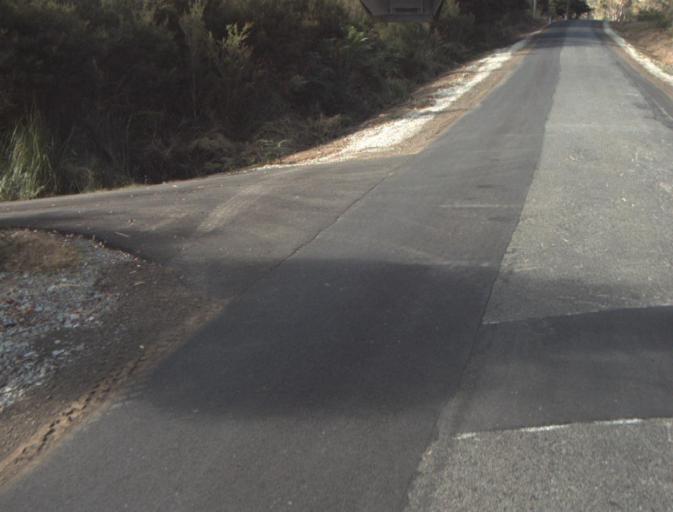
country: AU
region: Tasmania
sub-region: Launceston
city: Mayfield
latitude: -41.3088
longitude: 147.1988
